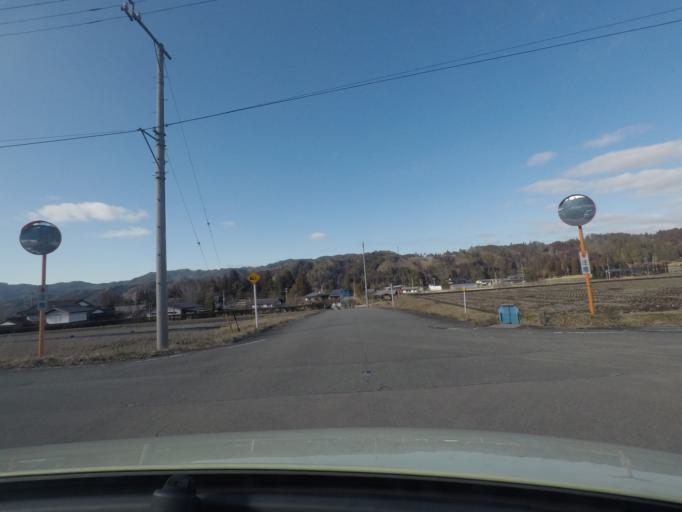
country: JP
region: Gifu
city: Takayama
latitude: 36.1674
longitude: 137.3260
